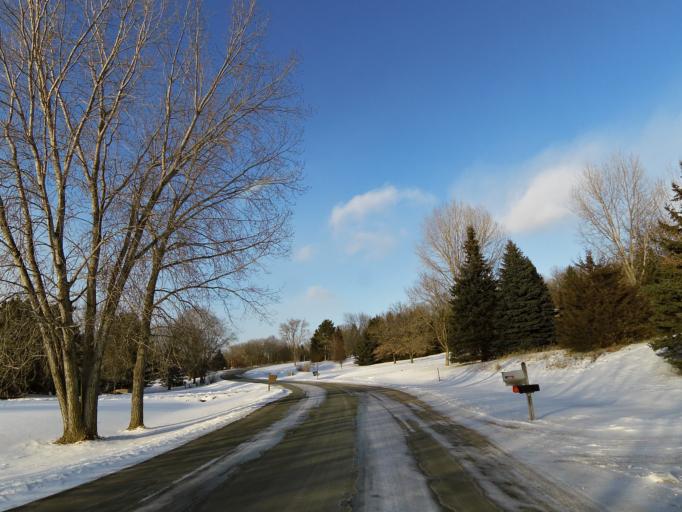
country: US
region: Minnesota
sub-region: Washington County
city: Lake Elmo
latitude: 44.9731
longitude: -92.8470
